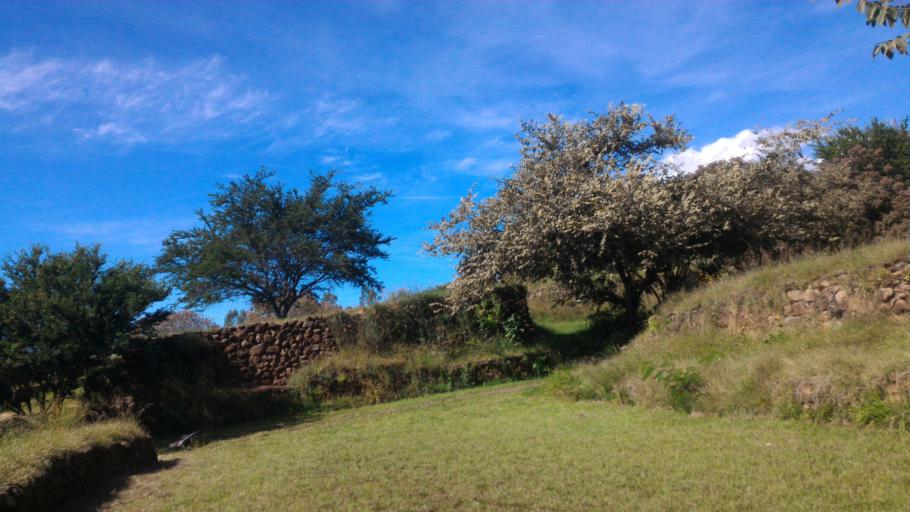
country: MX
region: Jalisco
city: Teuchitlan
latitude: 20.6953
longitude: -103.8359
